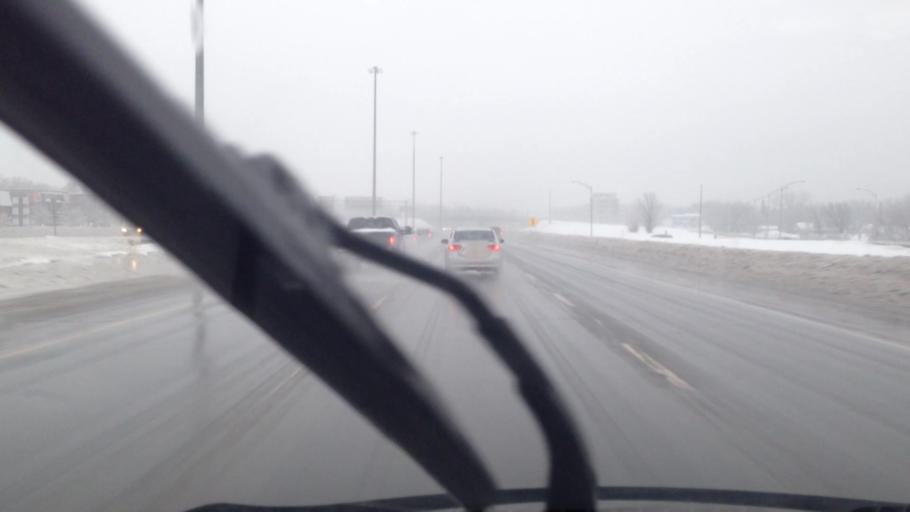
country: CA
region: Quebec
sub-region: Laurentides
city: Boisbriand
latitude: 45.6182
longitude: -73.8258
